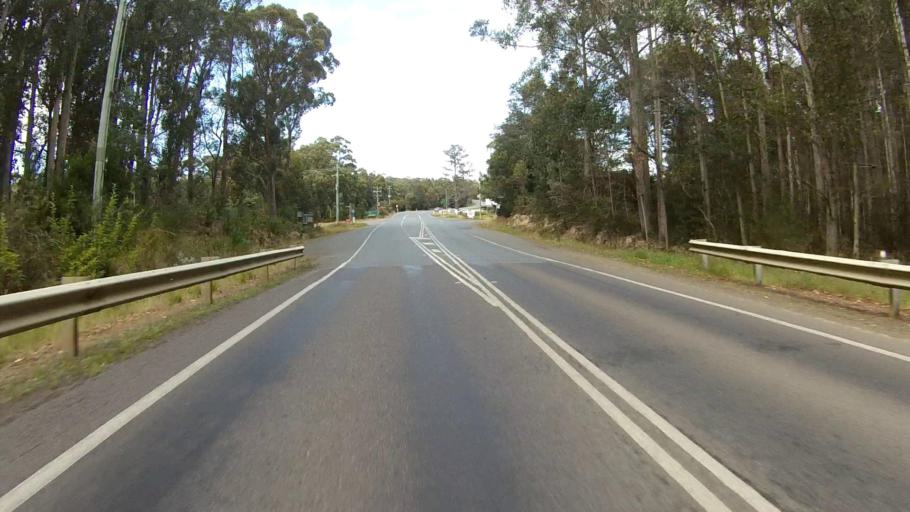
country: AU
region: Tasmania
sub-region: Kingborough
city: Kettering
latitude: -43.1055
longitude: 147.2452
